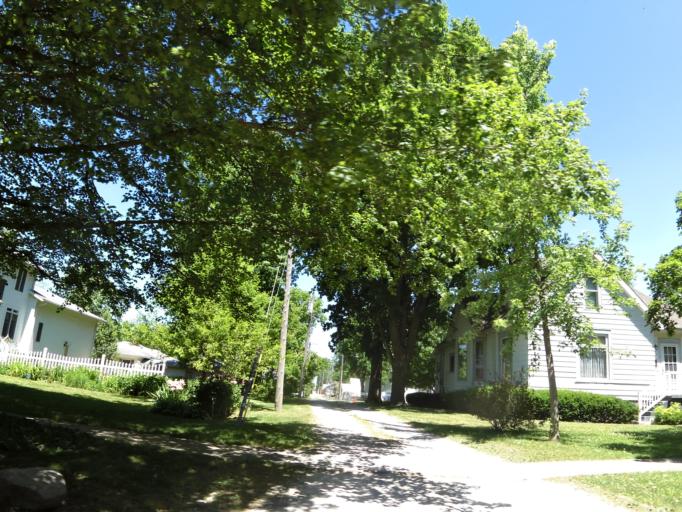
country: US
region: Illinois
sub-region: Iroquois County
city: Milford
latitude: 40.6284
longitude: -87.6925
